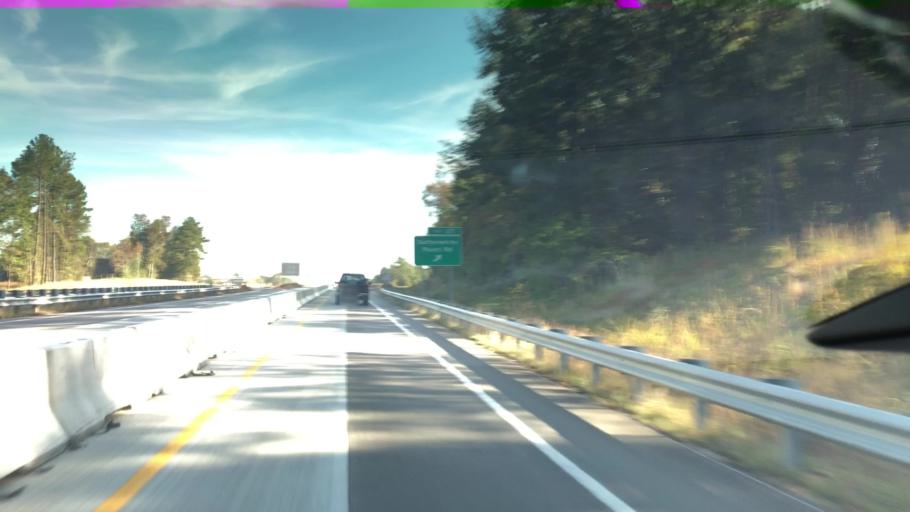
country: US
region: North Carolina
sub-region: Vance County
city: Henderson
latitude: 36.3587
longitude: -78.3789
